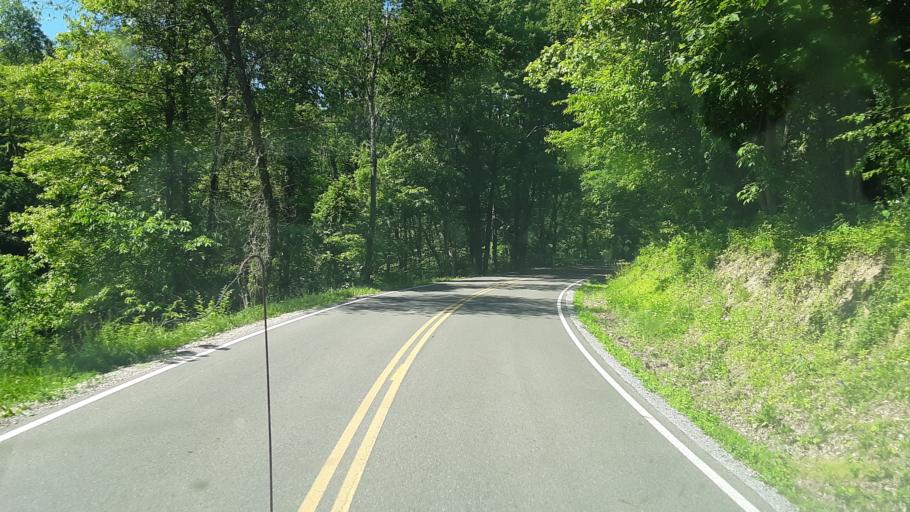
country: US
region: Ohio
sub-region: Coshocton County
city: Coshocton
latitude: 40.2334
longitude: -81.8174
